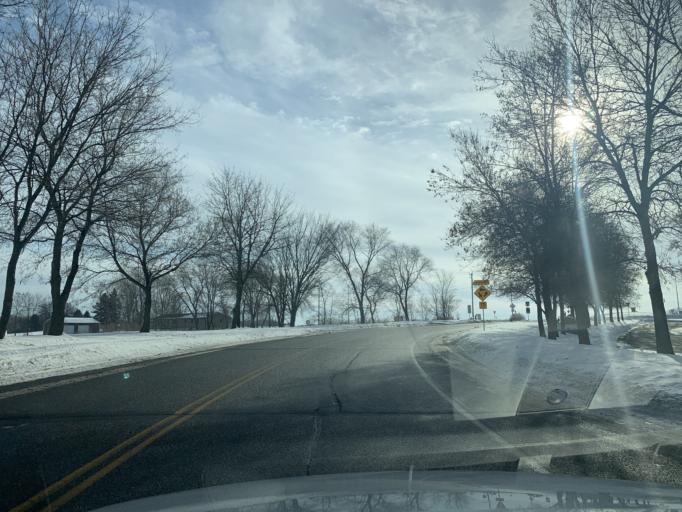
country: US
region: Minnesota
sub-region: Wright County
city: Albertville
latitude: 45.2254
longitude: -93.6441
